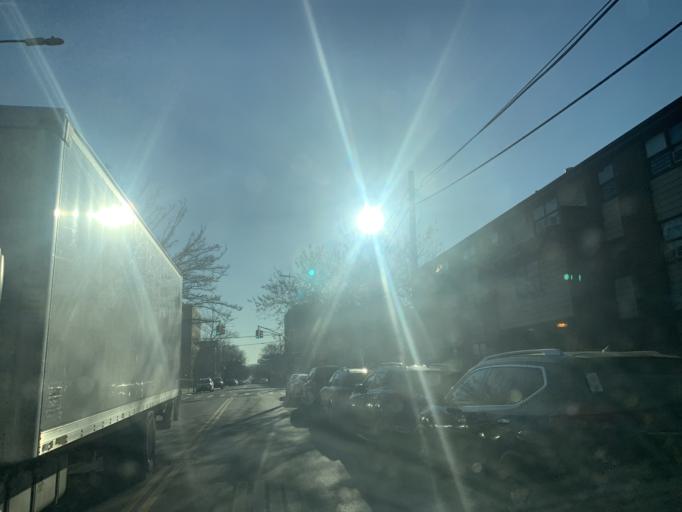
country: US
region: New York
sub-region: Kings County
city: East New York
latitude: 40.6978
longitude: -73.9206
